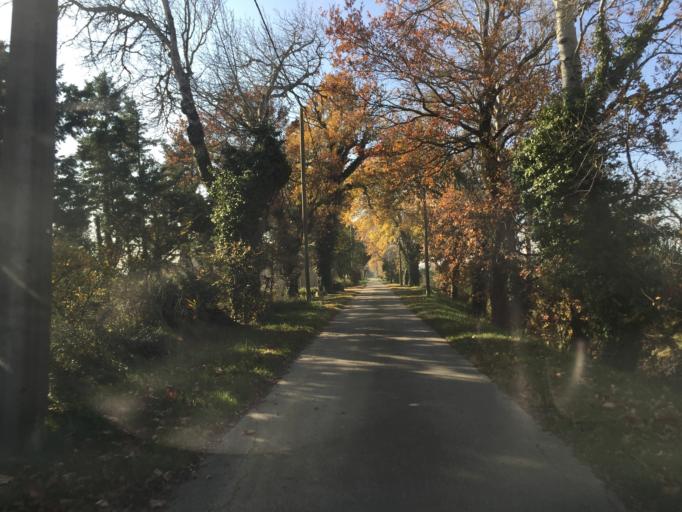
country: FR
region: Provence-Alpes-Cote d'Azur
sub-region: Departement du Vaucluse
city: Bedarrides
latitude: 44.0388
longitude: 4.9316
